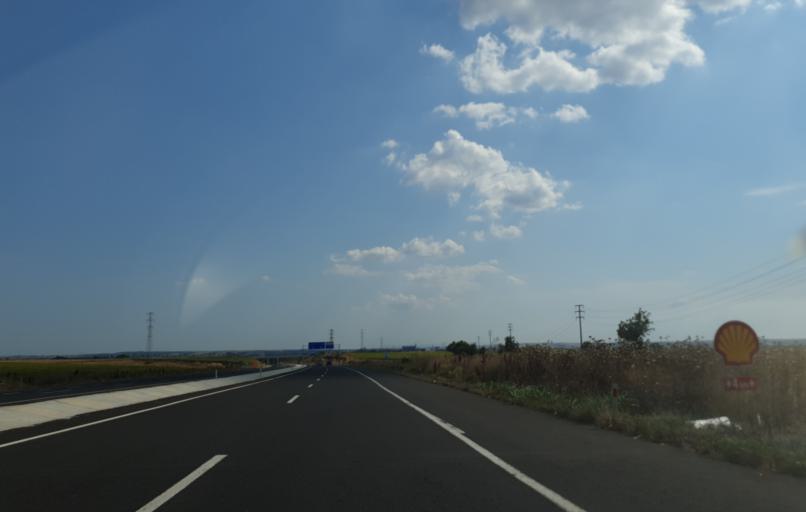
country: TR
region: Tekirdag
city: Muratli
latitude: 41.2313
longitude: 27.5332
